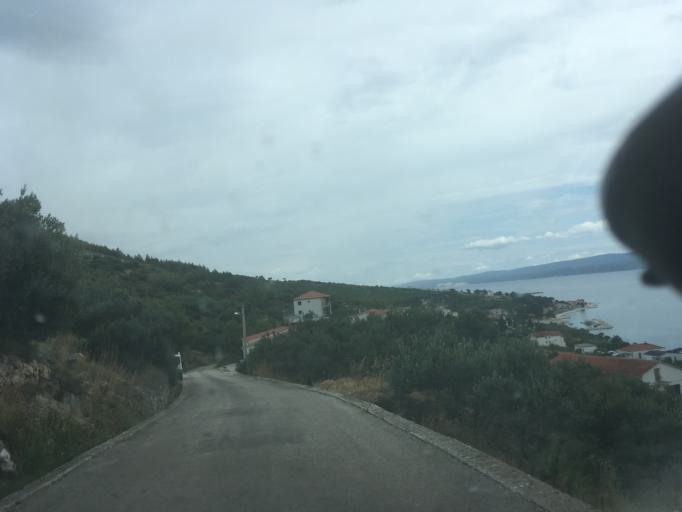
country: HR
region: Splitsko-Dalmatinska
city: Jesenice
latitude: 43.4580
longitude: 16.6191
